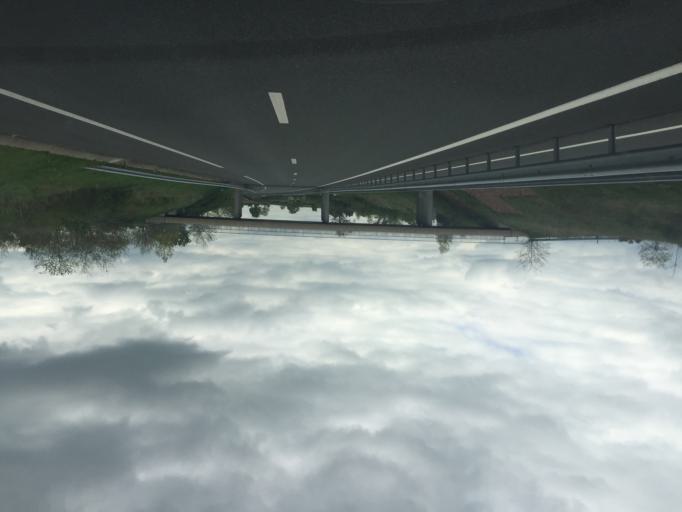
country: FR
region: Rhone-Alpes
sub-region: Departement de la Loire
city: La Pacaudiere
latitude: 46.1818
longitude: 3.8754
